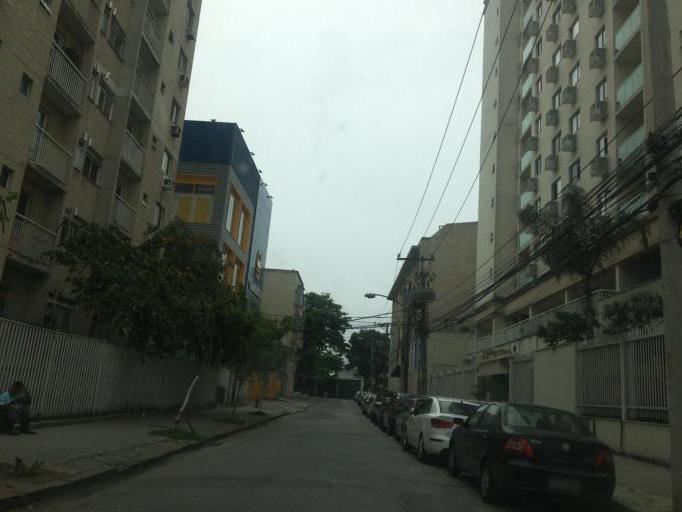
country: BR
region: Rio de Janeiro
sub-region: Rio De Janeiro
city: Rio de Janeiro
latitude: -22.8928
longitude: -43.2197
